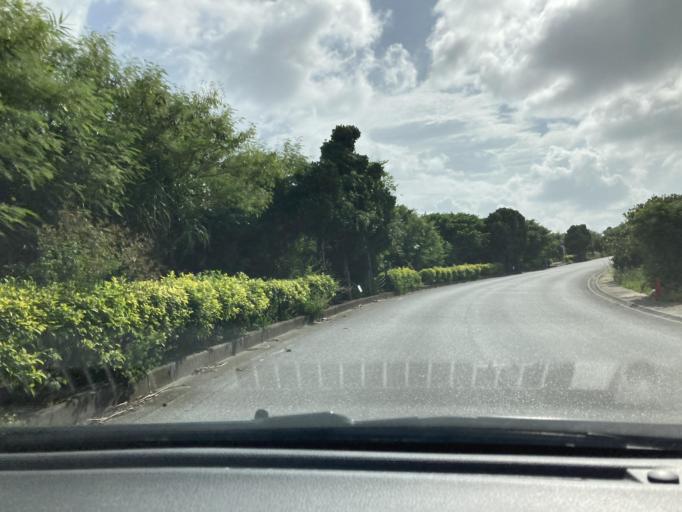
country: JP
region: Okinawa
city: Itoman
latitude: 26.0856
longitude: 127.6928
